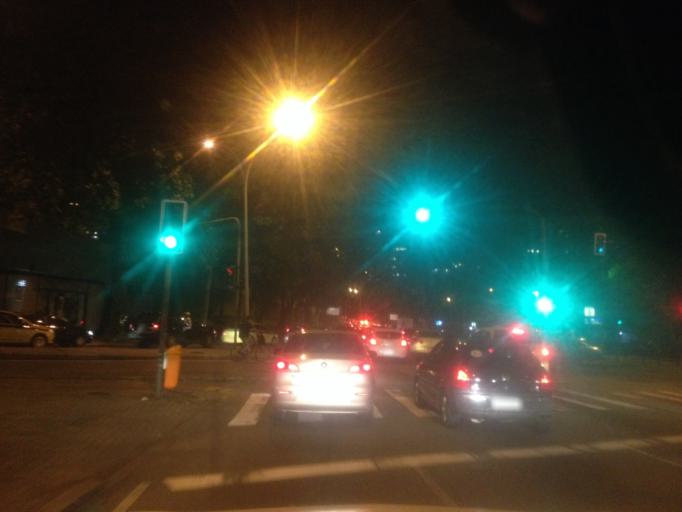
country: BR
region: Rio de Janeiro
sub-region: Rio De Janeiro
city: Rio de Janeiro
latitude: -22.9629
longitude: -43.2039
